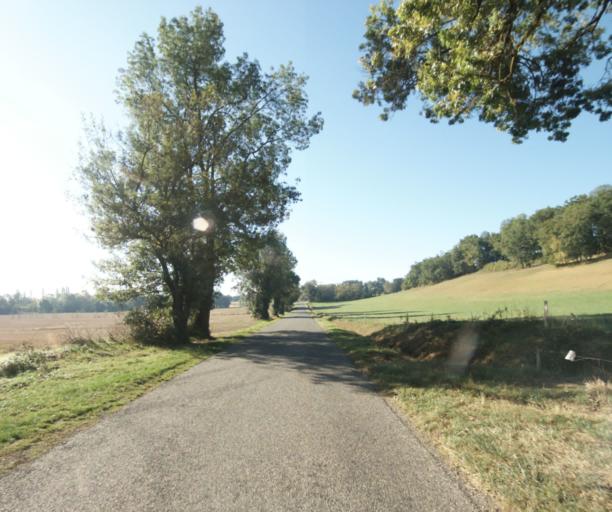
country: FR
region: Midi-Pyrenees
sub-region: Departement du Gers
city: Vic-Fezensac
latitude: 43.8224
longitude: 0.2881
